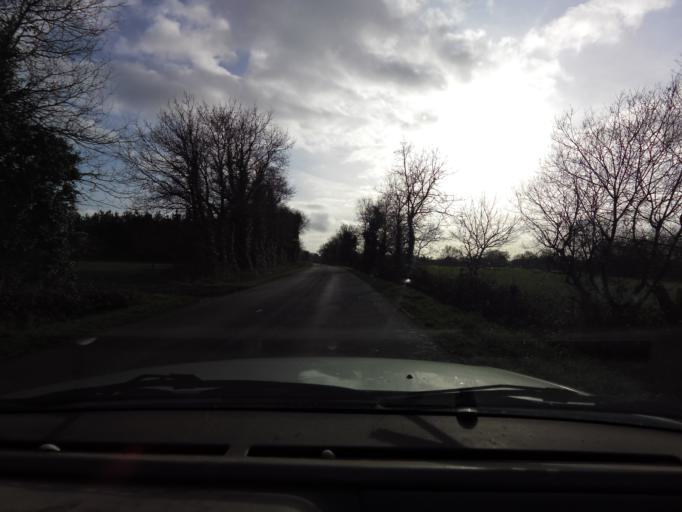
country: FR
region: Brittany
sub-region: Departement du Morbihan
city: Limerzel
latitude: 47.6647
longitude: -2.3590
